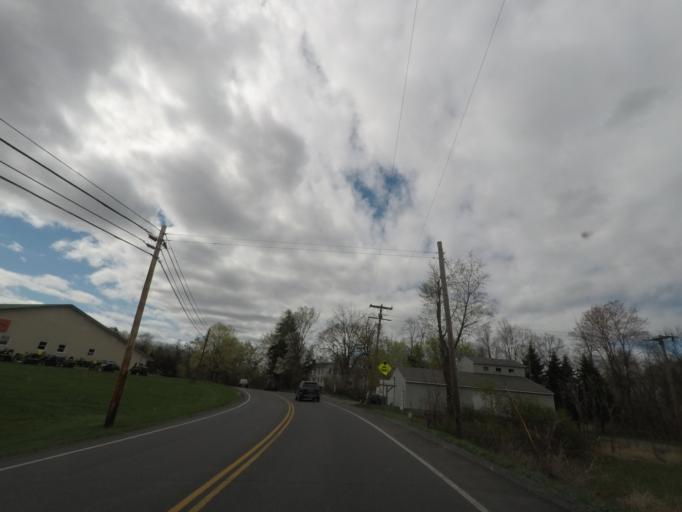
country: US
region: New York
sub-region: Columbia County
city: Chatham
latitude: 42.3733
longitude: -73.6231
